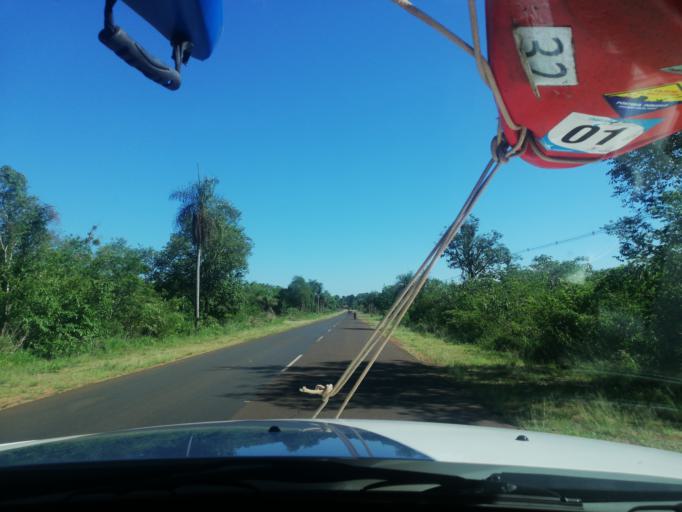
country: AR
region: Misiones
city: Santa Ana
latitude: -27.3447
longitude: -55.5842
